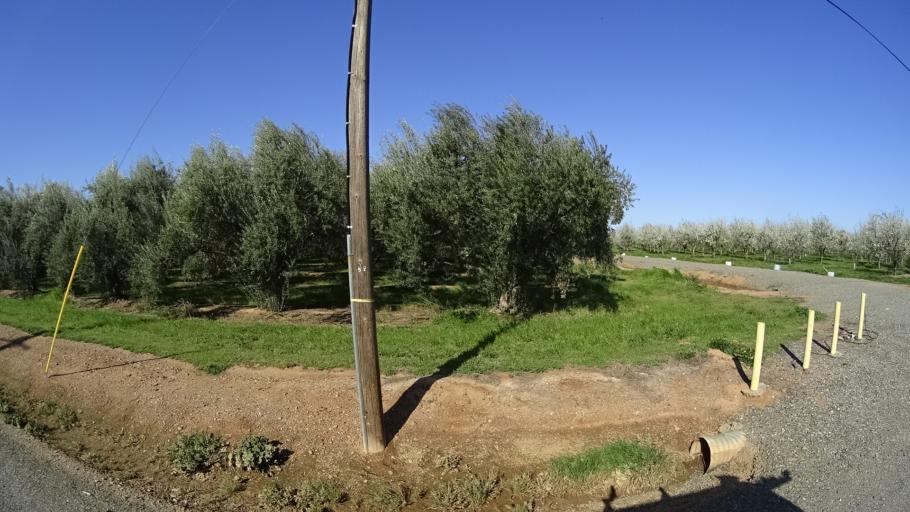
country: US
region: California
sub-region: Glenn County
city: Hamilton City
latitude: 39.7720
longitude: -122.0854
